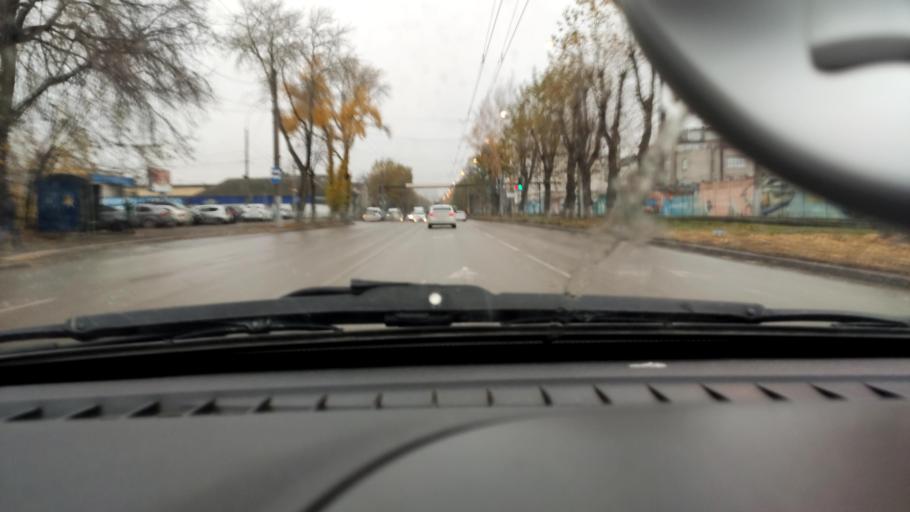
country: RU
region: Perm
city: Perm
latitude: 57.9744
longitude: 56.2464
